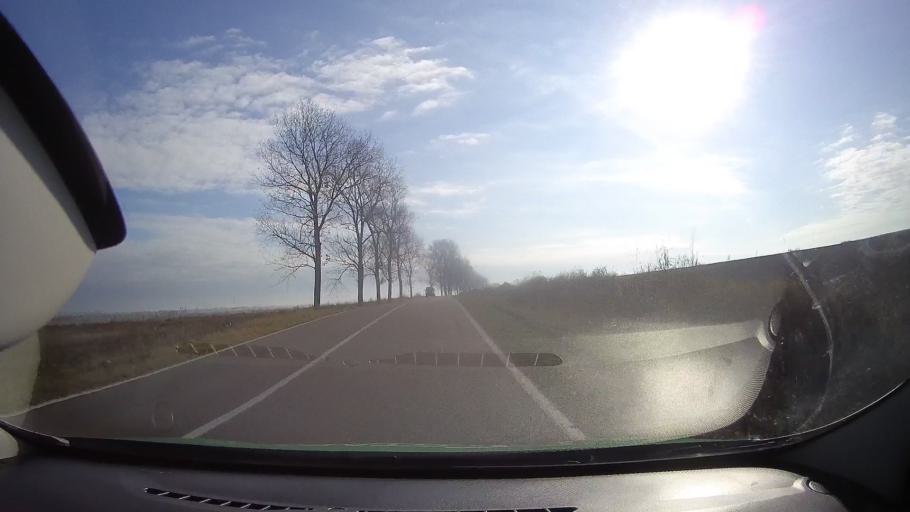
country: RO
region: Tulcea
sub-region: Comuna Mahmudia
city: Mahmudia
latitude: 45.0669
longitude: 29.1051
